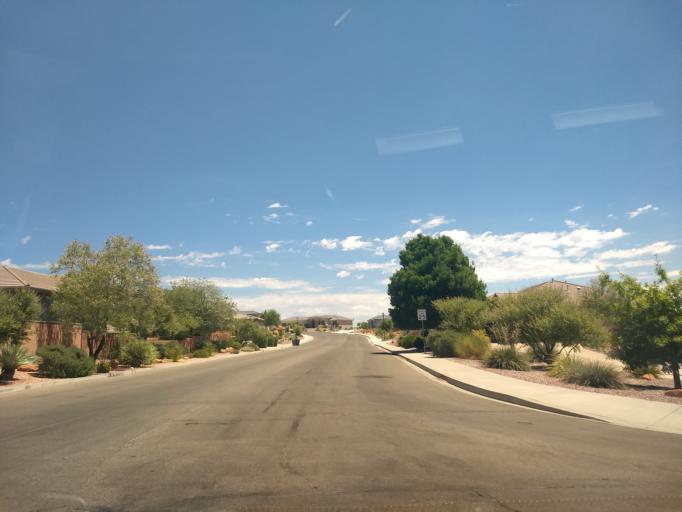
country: US
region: Utah
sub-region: Washington County
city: Washington
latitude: 37.1476
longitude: -113.5228
